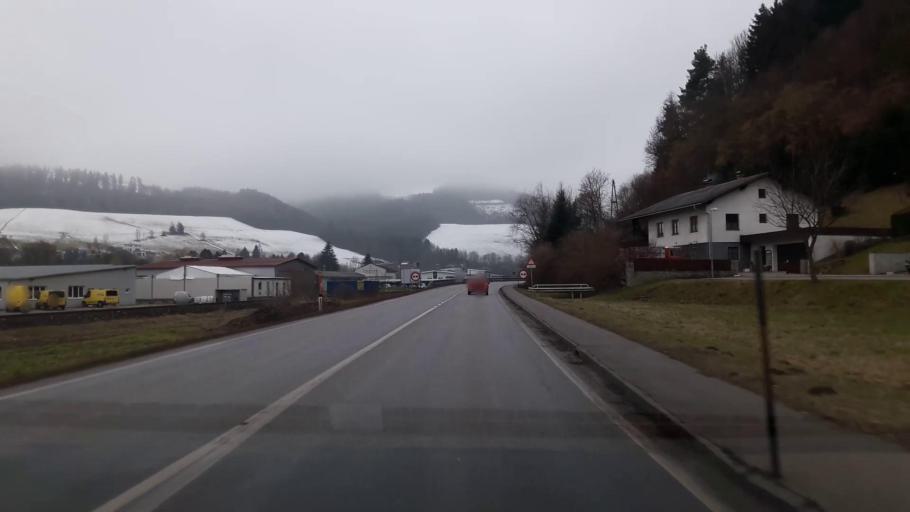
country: AT
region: Lower Austria
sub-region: Politischer Bezirk Neunkirchen
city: Grimmenstein
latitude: 47.6010
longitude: 16.1173
